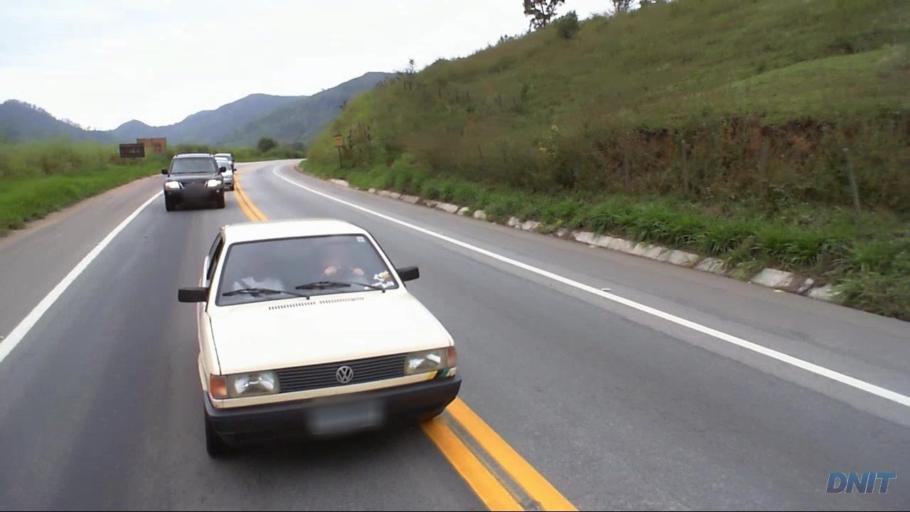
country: BR
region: Minas Gerais
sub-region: Timoteo
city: Timoteo
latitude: -19.6001
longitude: -42.7529
